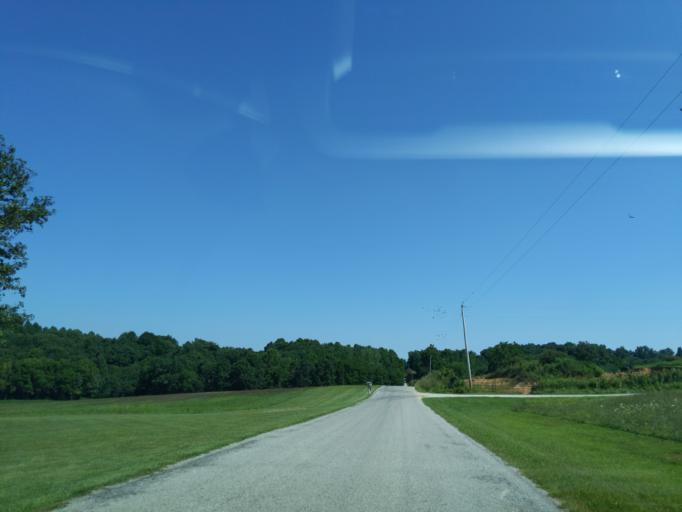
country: US
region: Indiana
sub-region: Ripley County
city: Osgood
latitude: 39.1006
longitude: -85.4323
